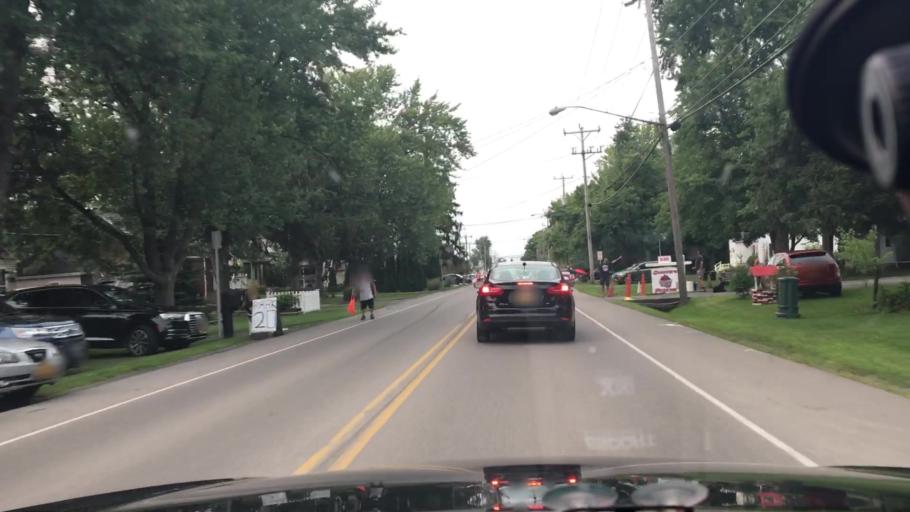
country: US
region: New York
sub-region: Erie County
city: Blasdell
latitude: 42.7648
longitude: -78.7922
